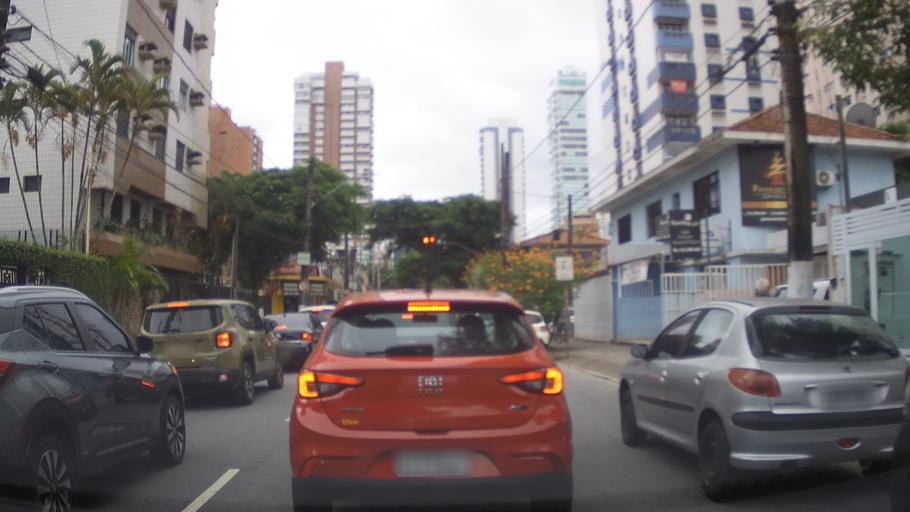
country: BR
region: Sao Paulo
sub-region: Santos
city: Santos
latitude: -23.9732
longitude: -46.3169
